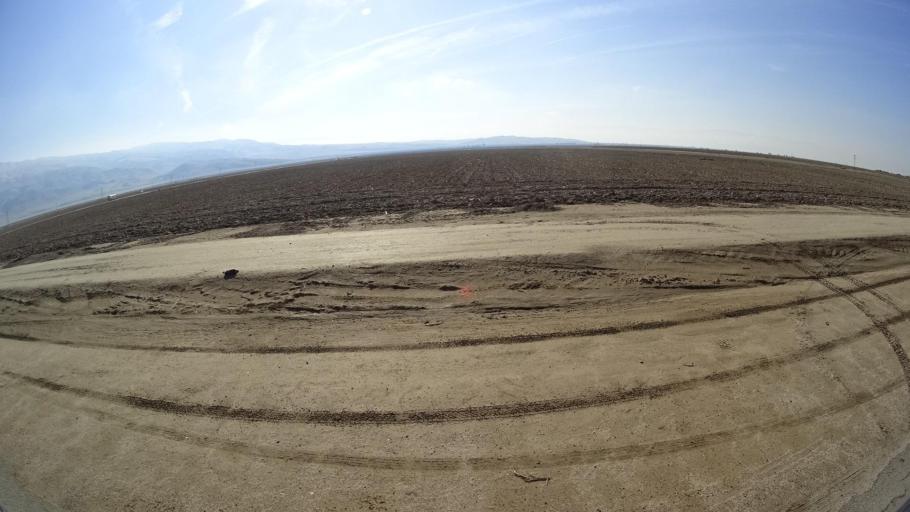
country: US
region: California
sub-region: Kern County
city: Arvin
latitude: 35.1946
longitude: -118.8122
